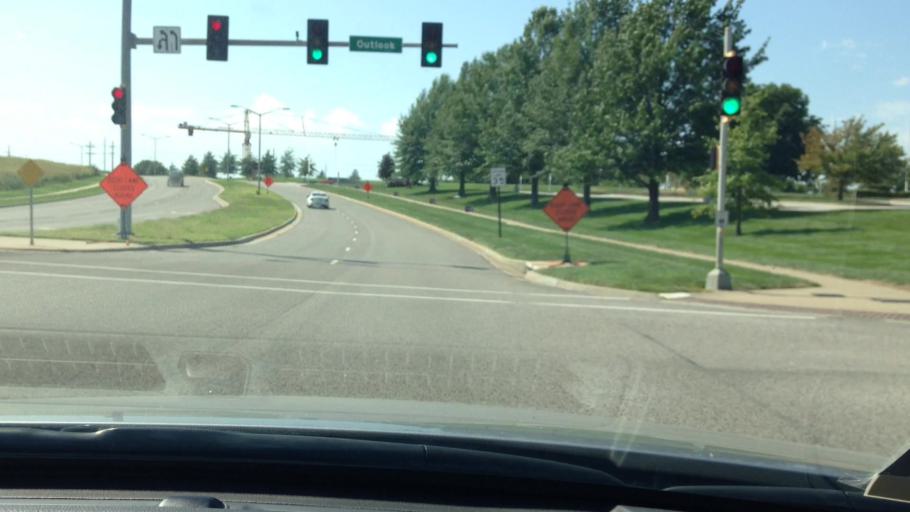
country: US
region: Kansas
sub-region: Johnson County
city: Leawood
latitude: 38.9221
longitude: -94.6542
